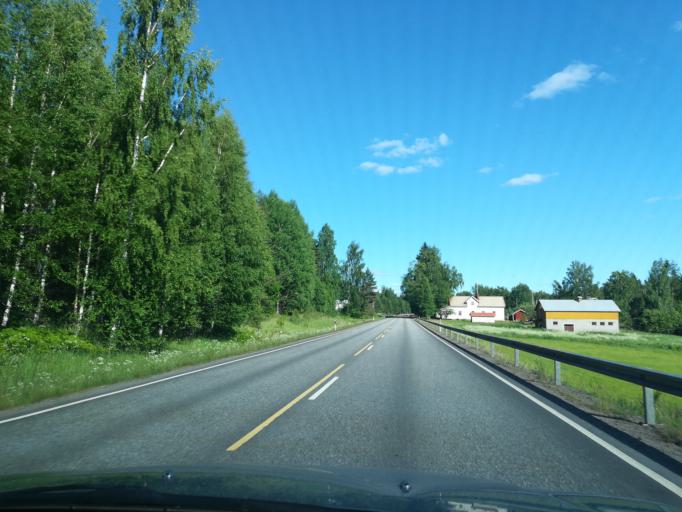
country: FI
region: South Karelia
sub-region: Imatra
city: Ruokolahti
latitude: 61.3730
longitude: 28.6647
